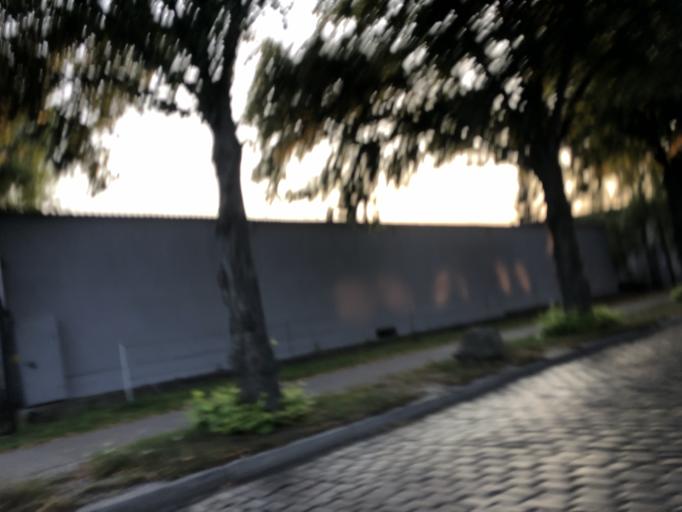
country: DE
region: Mecklenburg-Vorpommern
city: Rostock
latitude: 54.0743
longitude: 12.1390
